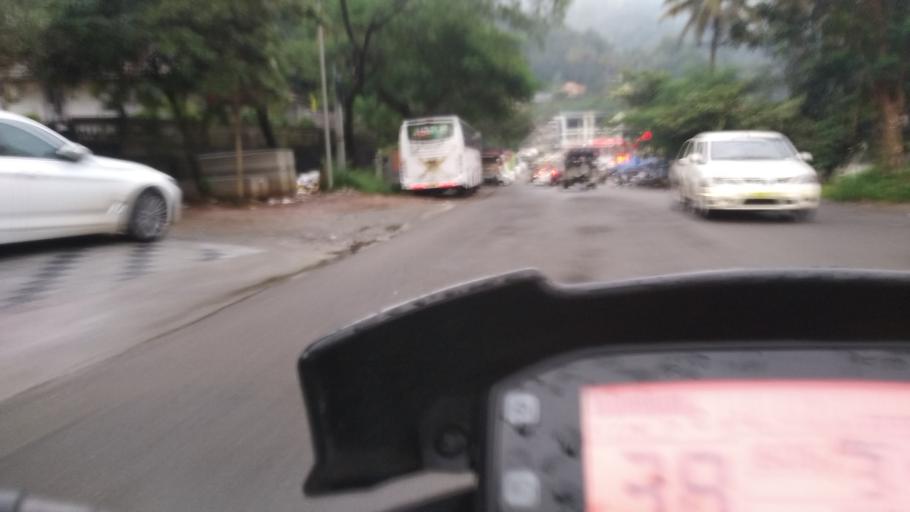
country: IN
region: Kerala
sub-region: Idukki
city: Munnar
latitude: 10.0147
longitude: 76.9510
